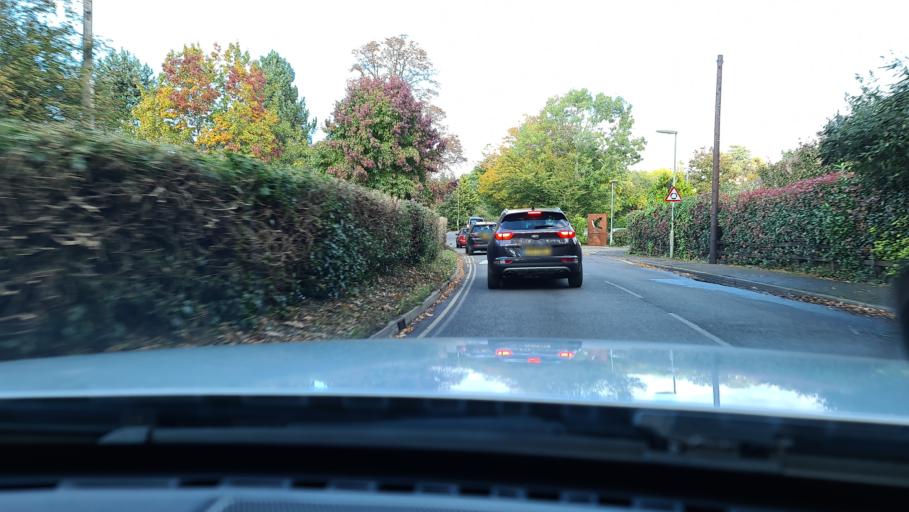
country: GB
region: England
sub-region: Surrey
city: Esher
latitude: 51.3667
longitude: -0.3778
